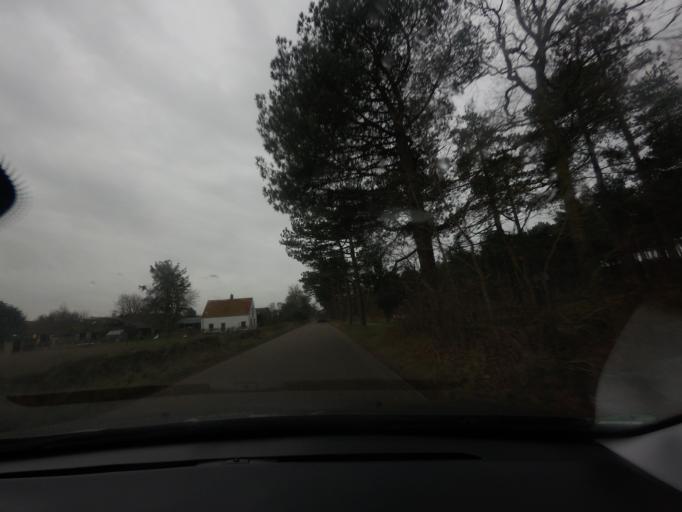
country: NL
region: North Holland
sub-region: Gemeente Texel
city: Den Burg
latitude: 53.0874
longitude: 4.7546
